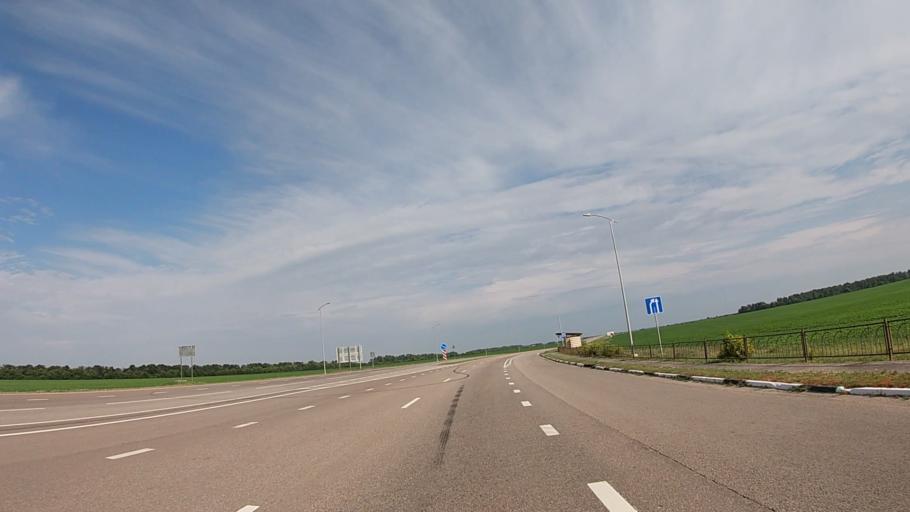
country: RU
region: Belgorod
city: Rakitnoye
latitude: 50.7918
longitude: 35.8666
